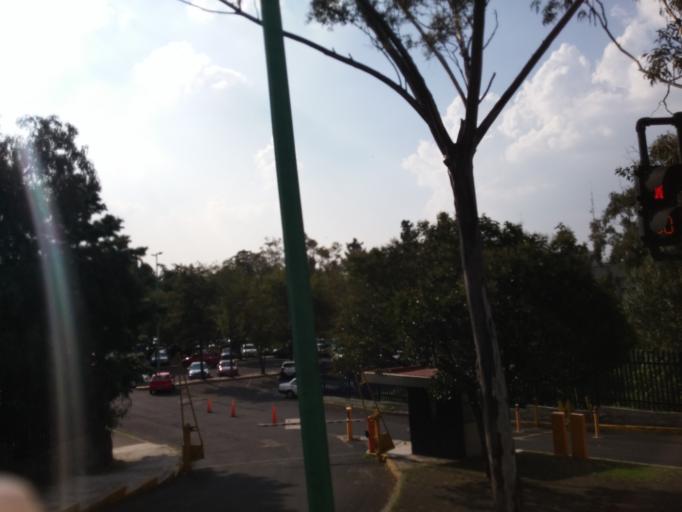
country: MX
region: Mexico City
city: Coyoacan
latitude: 19.3253
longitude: -99.1753
